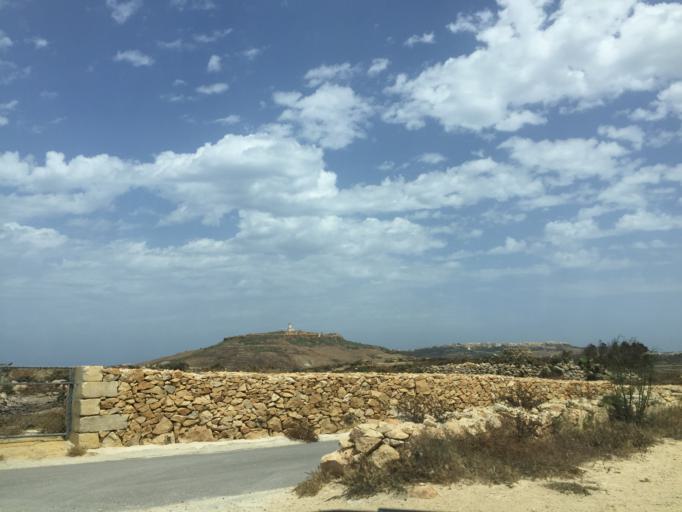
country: MT
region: L-Gharb
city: Gharb
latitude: 36.0712
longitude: 14.2046
